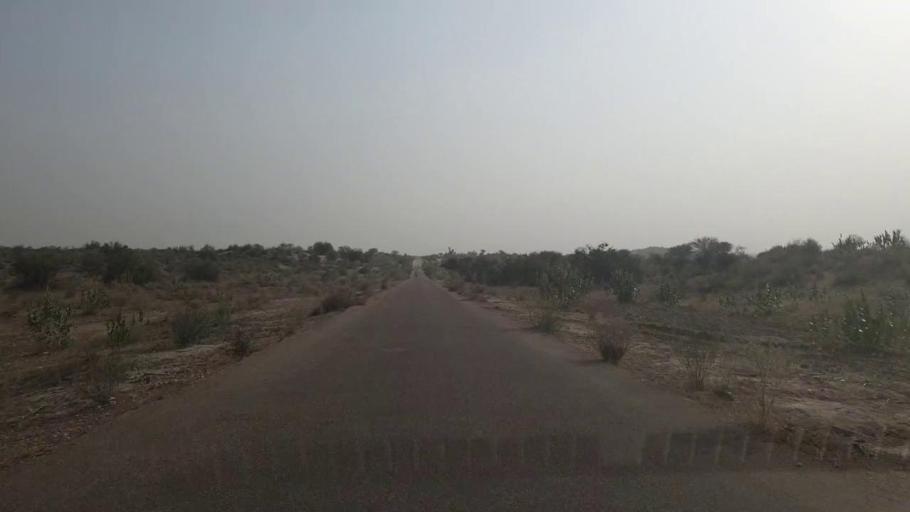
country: PK
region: Sindh
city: Chor
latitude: 25.4642
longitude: 69.9672
